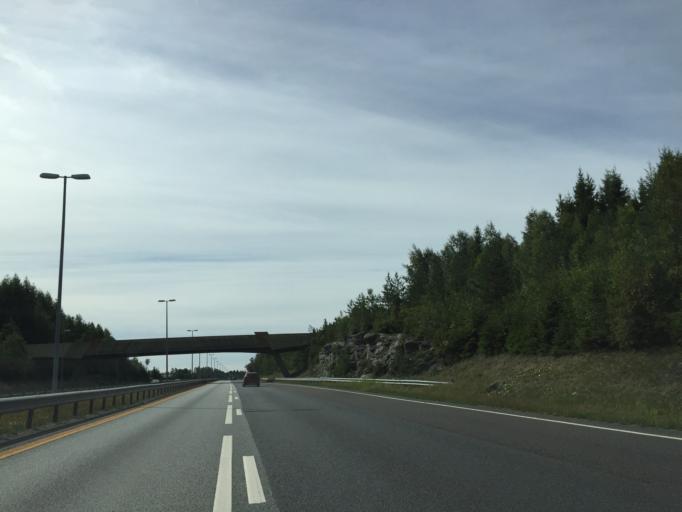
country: NO
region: Akershus
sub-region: Vestby
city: Vestby
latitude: 59.6463
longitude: 10.7401
